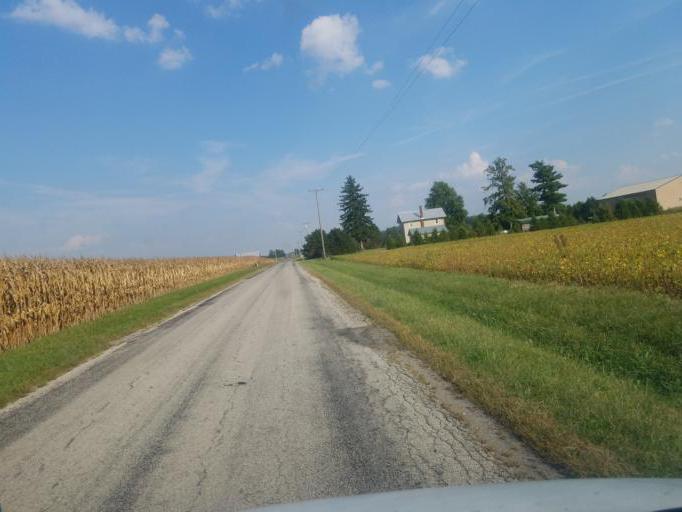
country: US
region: Ohio
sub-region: Hardin County
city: Forest
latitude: 40.9052
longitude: -83.5183
